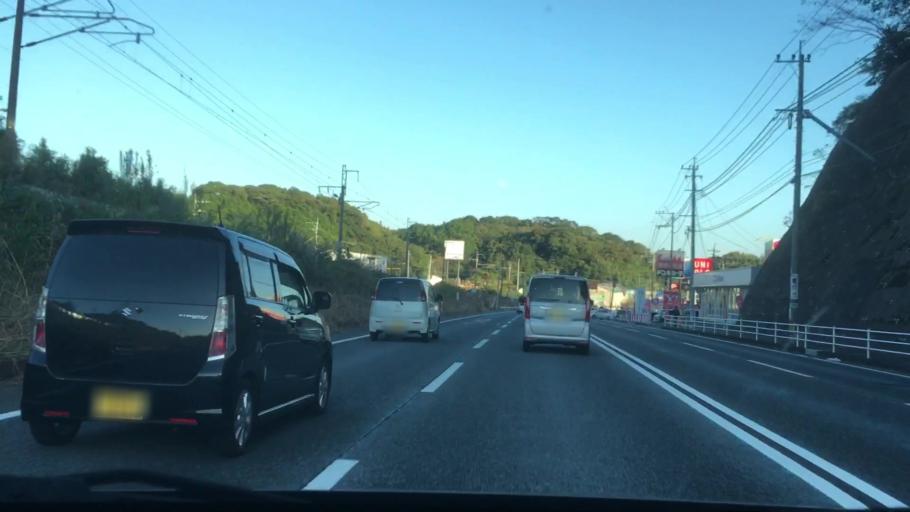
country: JP
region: Nagasaki
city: Sasebo
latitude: 33.1529
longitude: 129.7766
